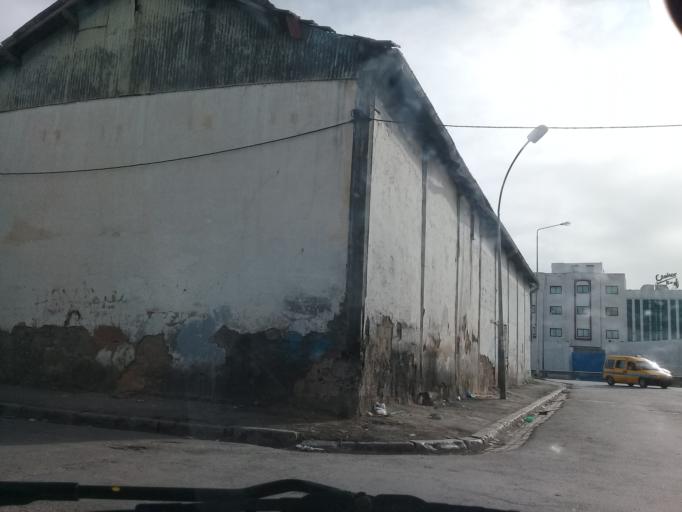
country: TN
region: Tunis
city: Tunis
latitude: 36.7920
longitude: 10.1857
